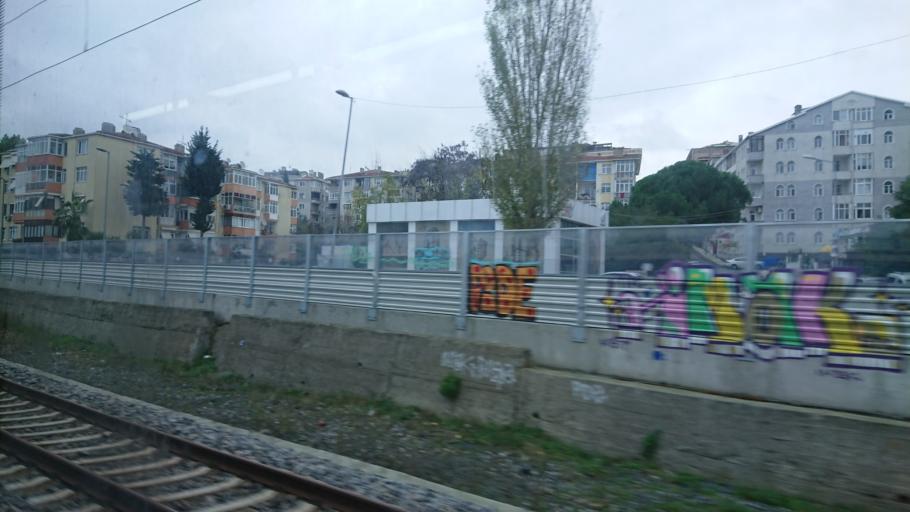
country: TR
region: Istanbul
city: Mahmutbey
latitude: 41.0013
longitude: 28.7687
